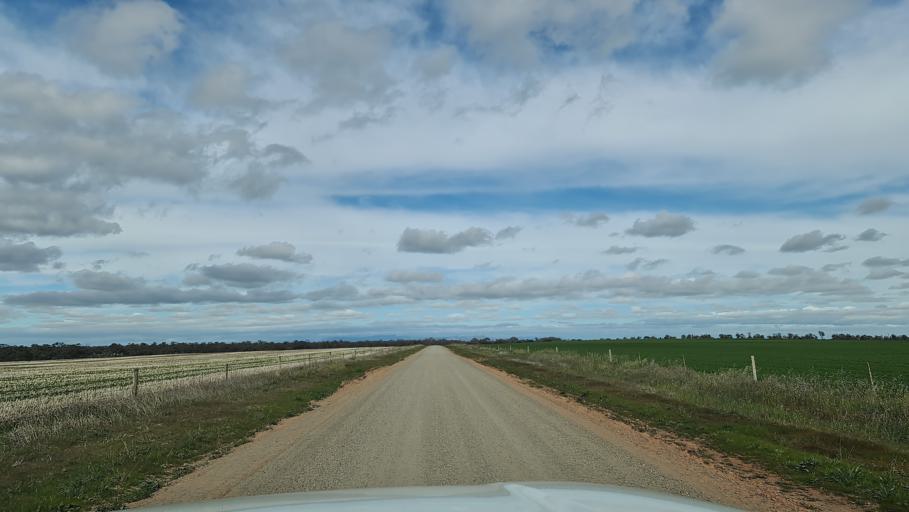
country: AU
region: Victoria
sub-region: Horsham
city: Horsham
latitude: -36.6223
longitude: 142.4117
